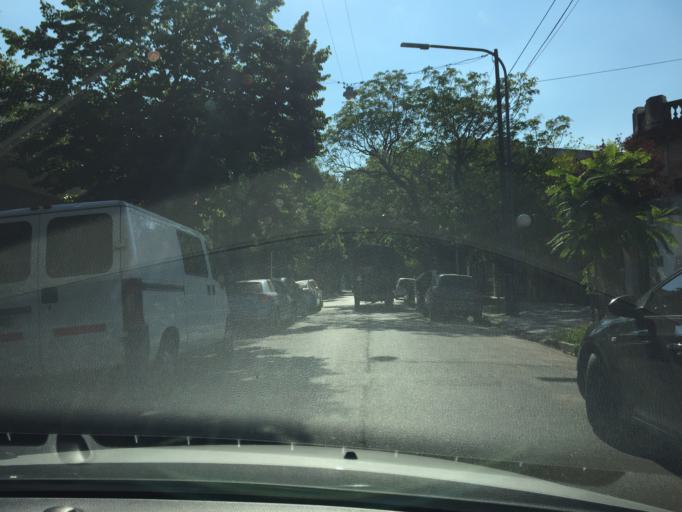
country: AR
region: Buenos Aires
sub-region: Partido de General San Martin
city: General San Martin
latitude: -34.5984
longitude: -58.5211
